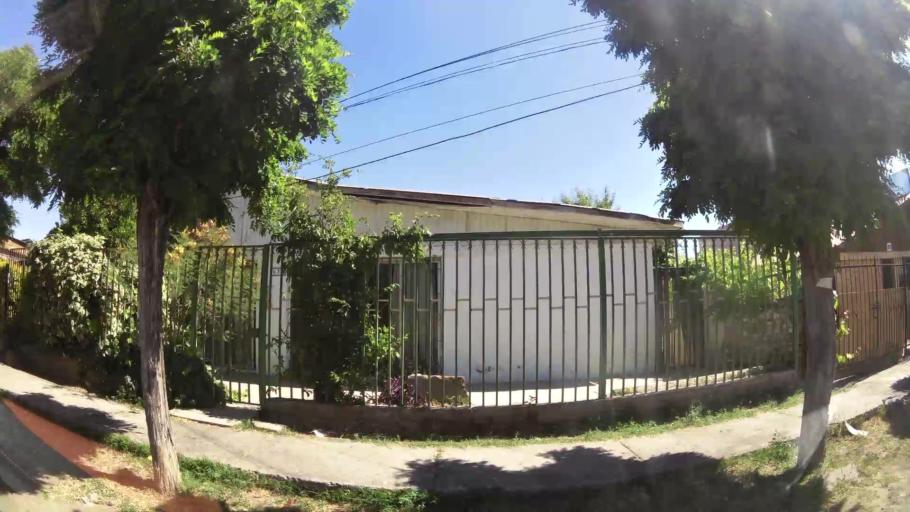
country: CL
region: Santiago Metropolitan
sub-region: Provincia de Maipo
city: San Bernardo
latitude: -33.5816
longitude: -70.6818
